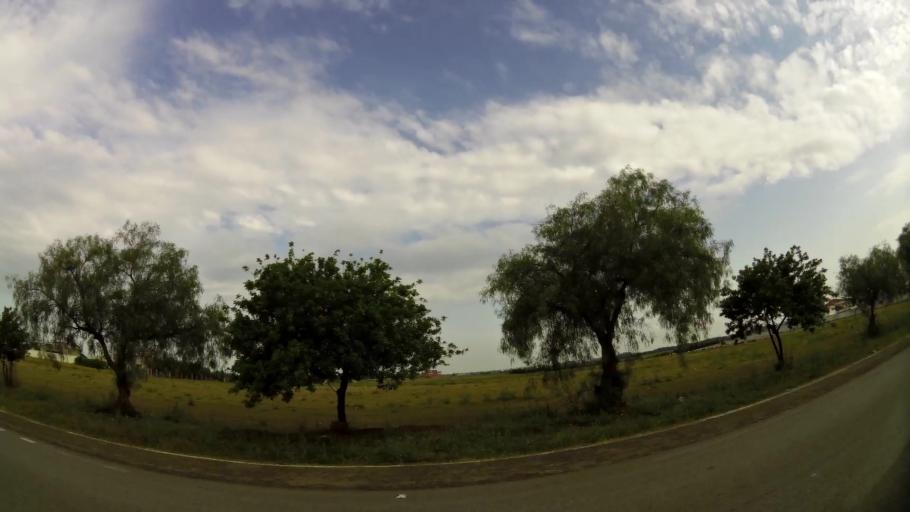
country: MA
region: Rabat-Sale-Zemmour-Zaer
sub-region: Khemisset
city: Khemisset
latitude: 33.8026
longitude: -6.0948
